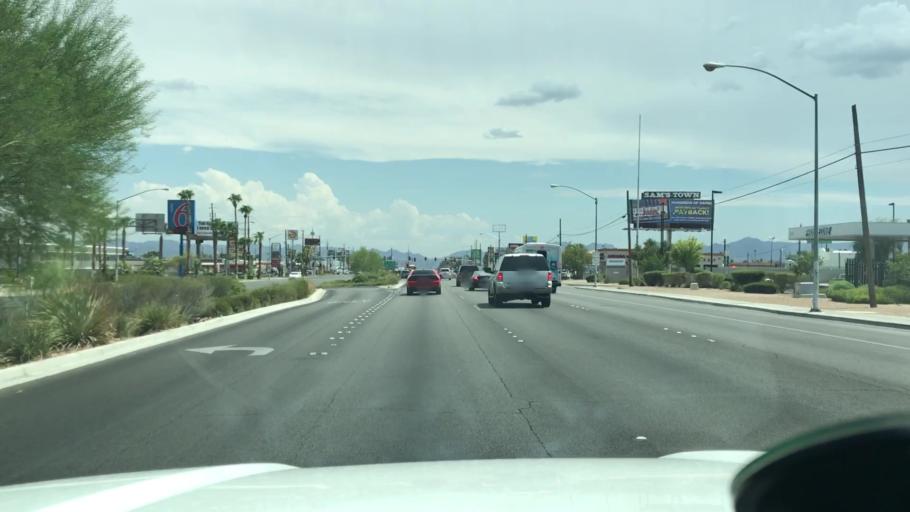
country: US
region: Nevada
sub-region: Clark County
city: Winchester
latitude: 36.1320
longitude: -115.0862
